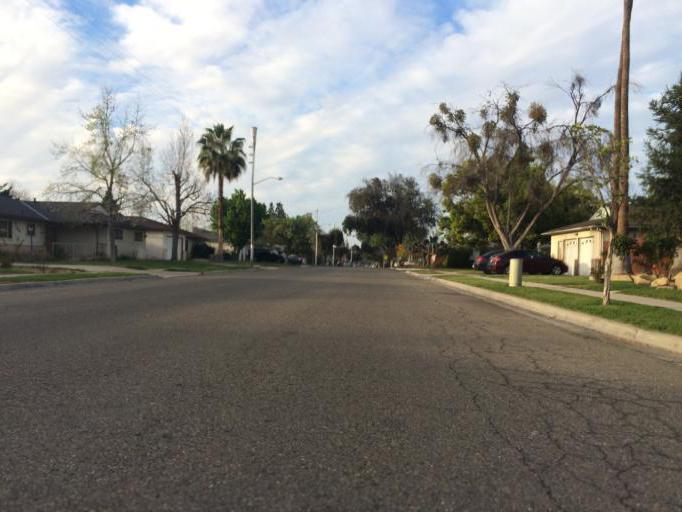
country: US
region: California
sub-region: Fresno County
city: Clovis
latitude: 36.8253
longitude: -119.7632
